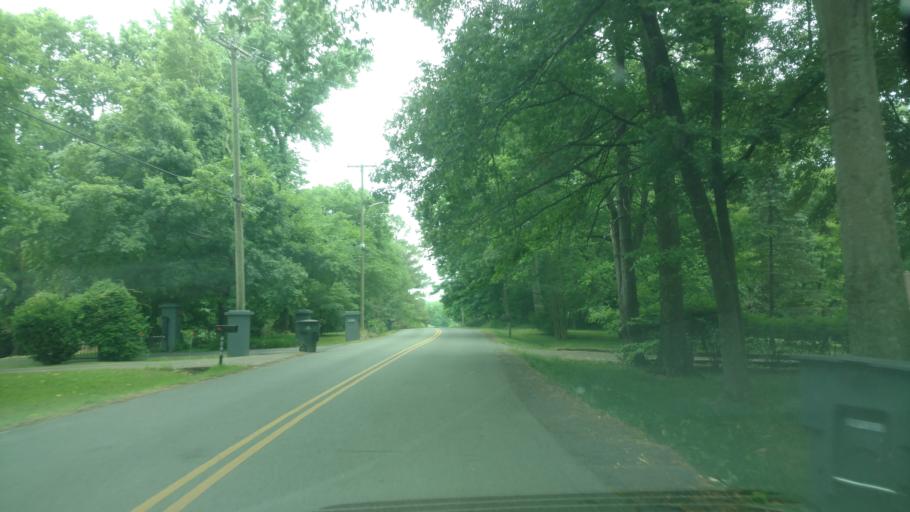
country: US
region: Tennessee
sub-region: Davidson County
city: Lakewood
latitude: 36.2081
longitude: -86.7019
